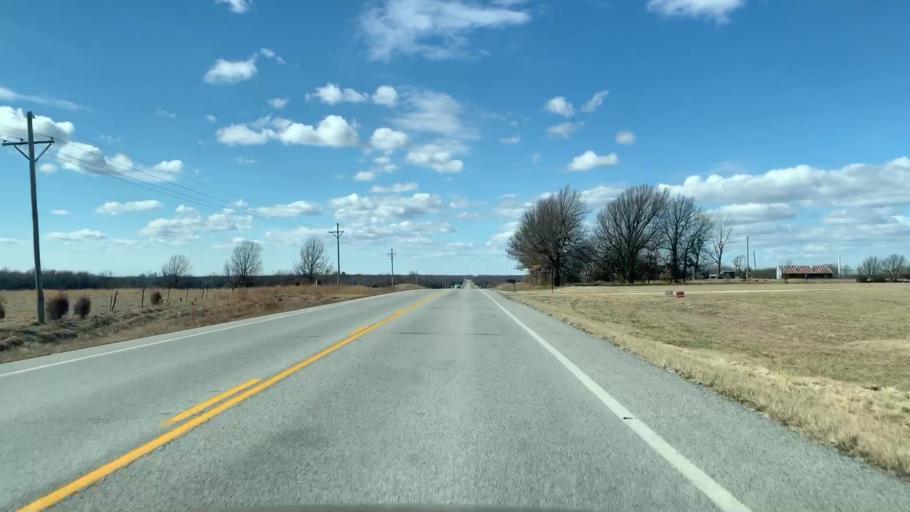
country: US
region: Kansas
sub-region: Cherokee County
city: Columbus
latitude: 37.1781
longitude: -94.7866
